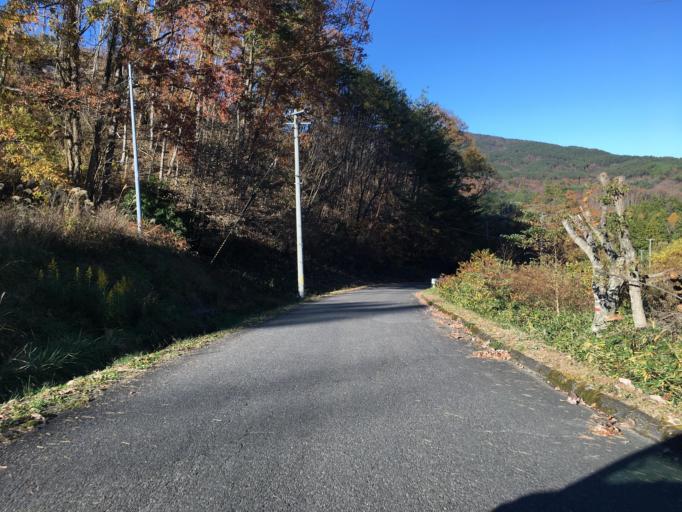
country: JP
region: Fukushima
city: Ishikawa
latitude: 37.2403
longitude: 140.5298
